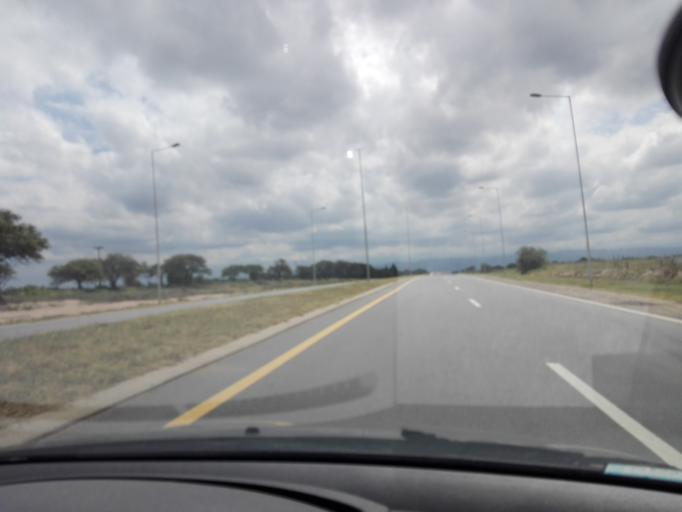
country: AR
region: Cordoba
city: Alta Gracia
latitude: -31.6521
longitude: -64.3175
